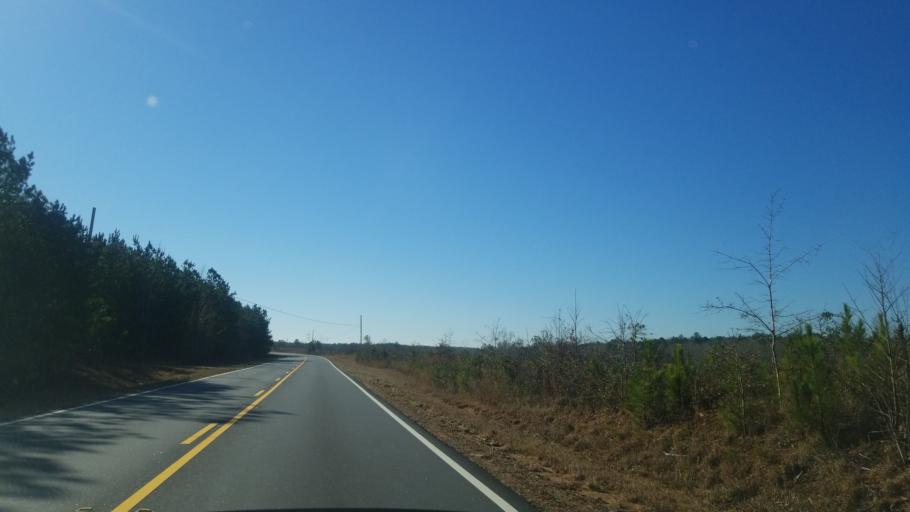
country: US
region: Alabama
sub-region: Chambers County
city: Valley
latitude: 32.7616
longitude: -85.0798
